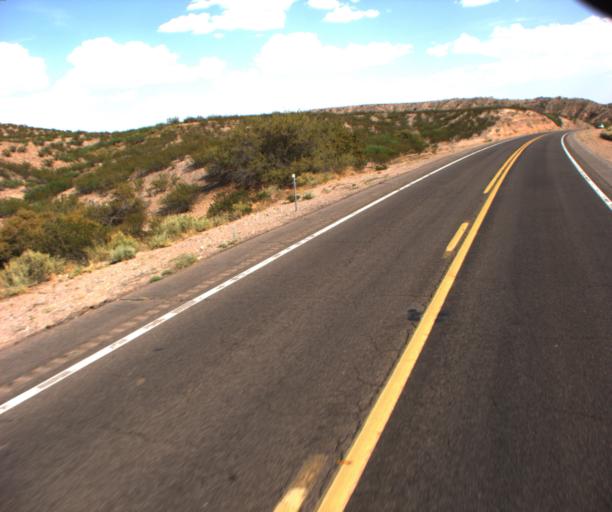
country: US
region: Arizona
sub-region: Greenlee County
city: Clifton
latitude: 32.8113
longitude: -109.1685
